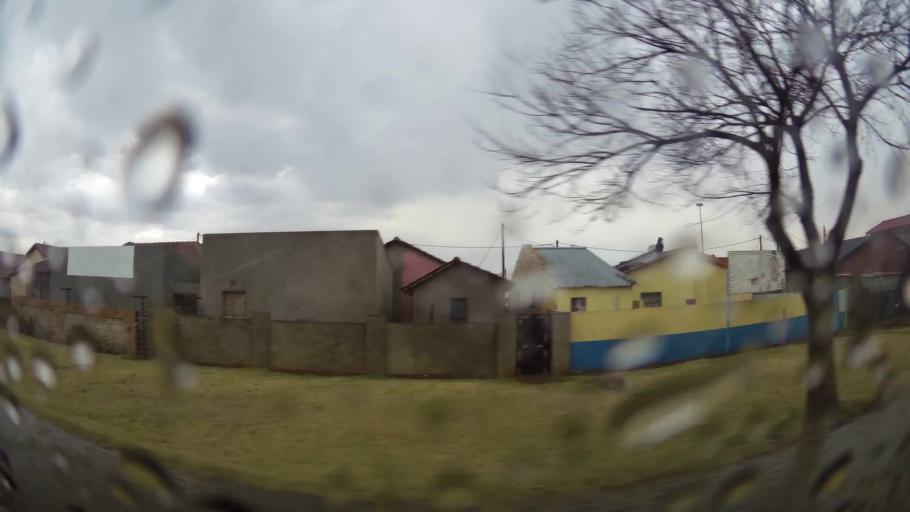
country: ZA
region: Gauteng
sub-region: Ekurhuleni Metropolitan Municipality
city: Germiston
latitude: -26.3606
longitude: 28.1367
